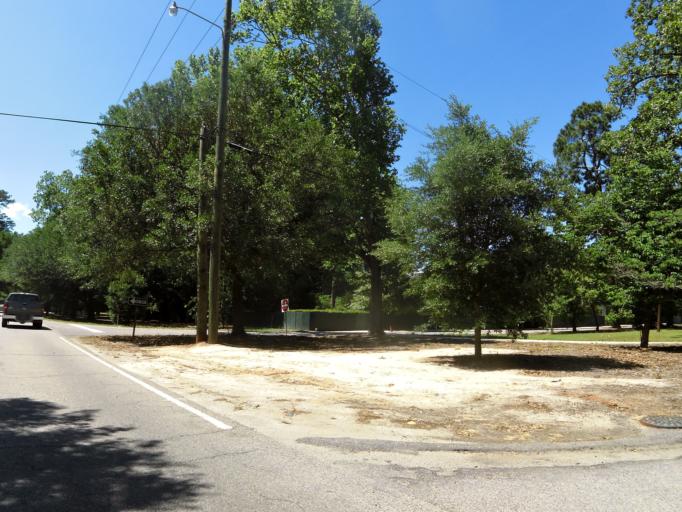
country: US
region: South Carolina
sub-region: Aiken County
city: Aiken
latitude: 33.5533
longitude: -81.7178
